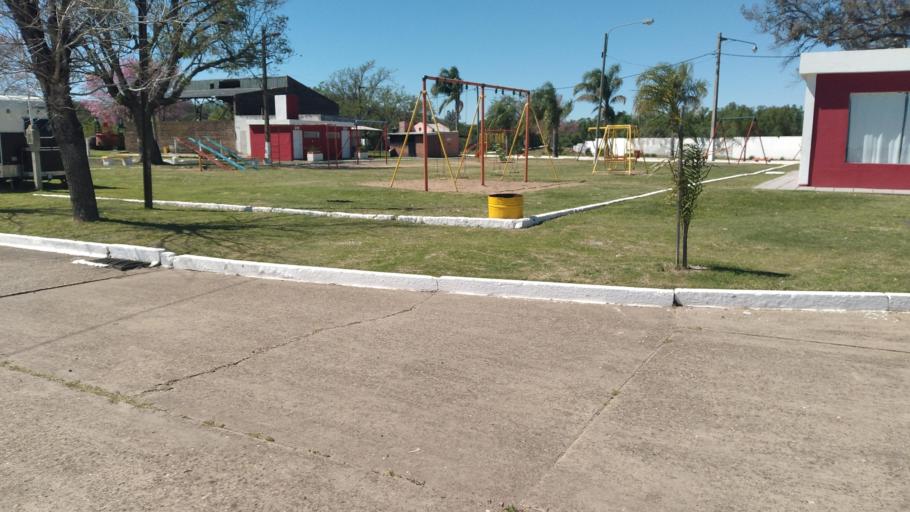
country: AR
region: Entre Rios
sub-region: Departamento de La Paz
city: La Paz
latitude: -30.7333
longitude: -59.6393
